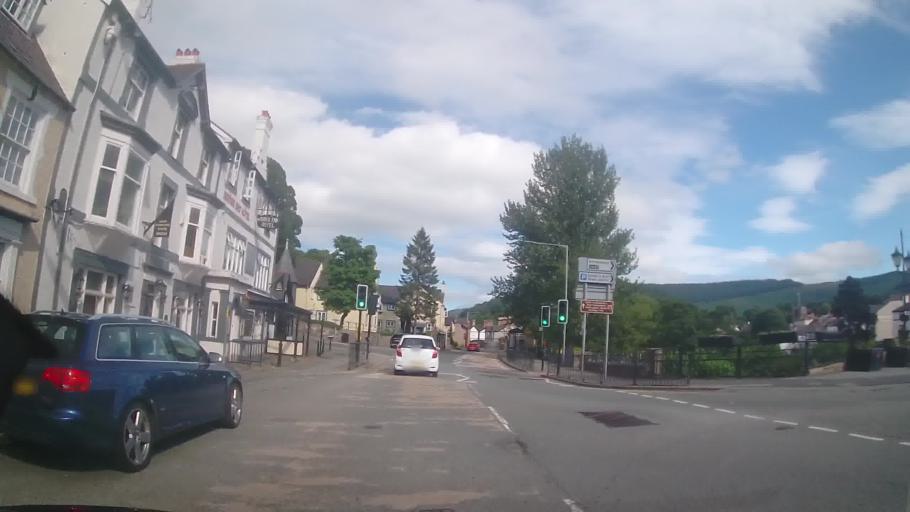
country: GB
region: Wales
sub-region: Denbighshire
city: Llangollen
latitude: 52.9722
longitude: -3.1702
